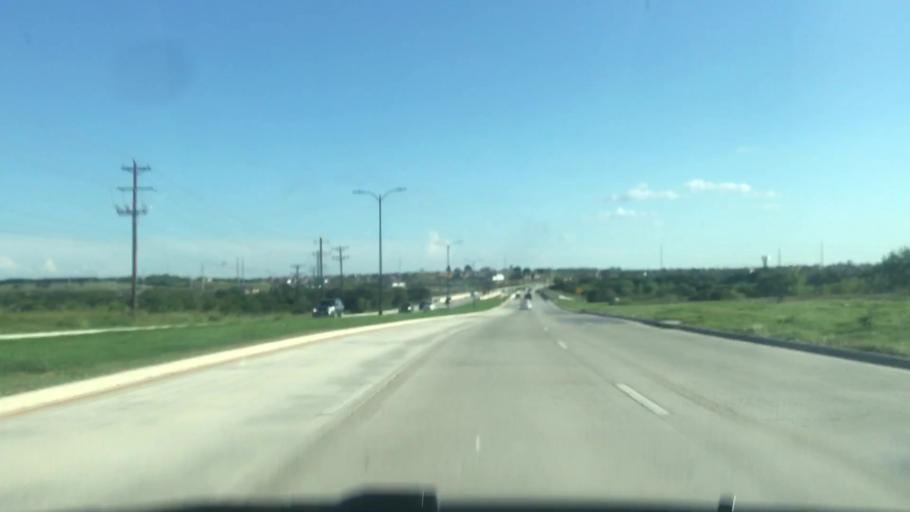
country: US
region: Texas
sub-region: Denton County
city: Little Elm
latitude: 33.2096
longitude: -96.8805
